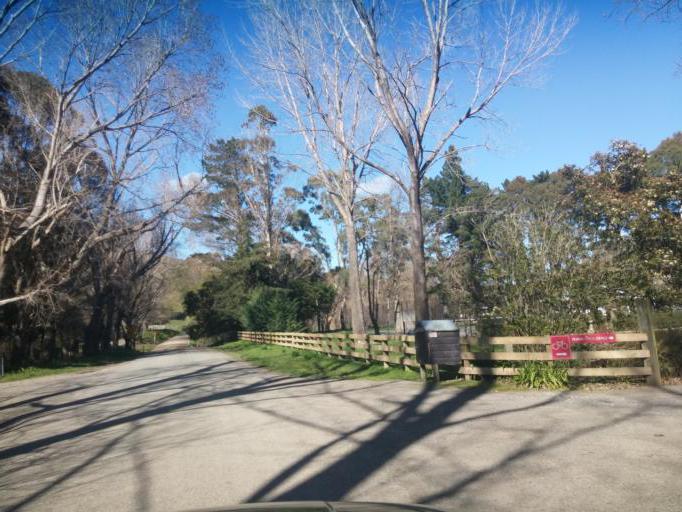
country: NZ
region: Wellington
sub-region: South Wairarapa District
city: Waipawa
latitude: -41.4430
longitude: 175.5225
